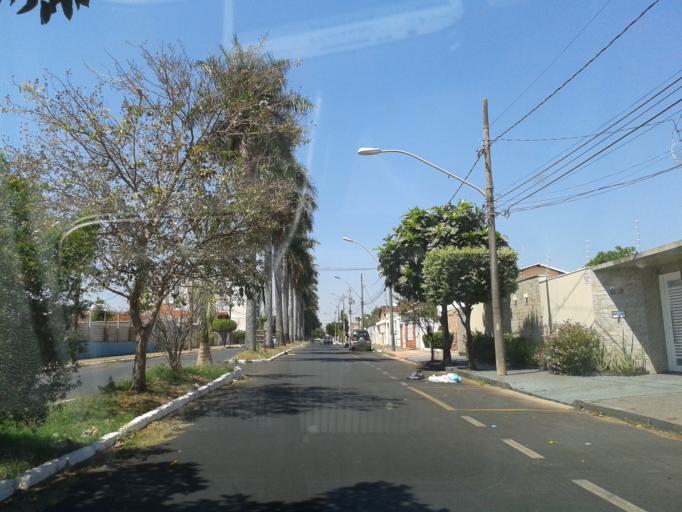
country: BR
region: Minas Gerais
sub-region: Araguari
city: Araguari
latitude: -18.6572
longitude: -48.1890
